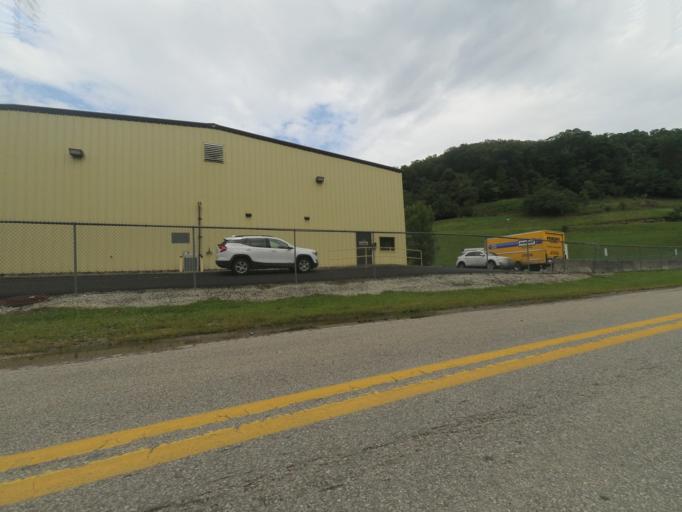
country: US
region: West Virginia
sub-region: Cabell County
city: Huntington
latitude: 38.3968
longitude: -82.4583
